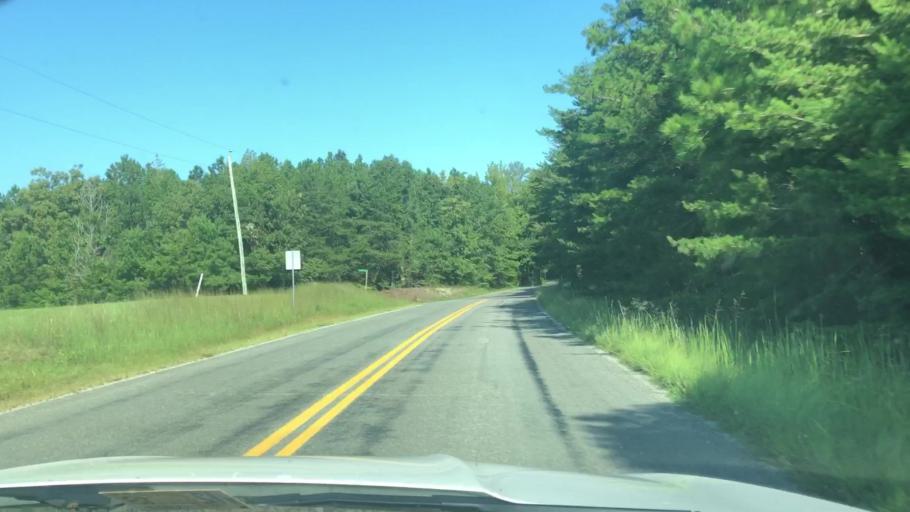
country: US
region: Virginia
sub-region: New Kent County
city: New Kent
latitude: 37.4864
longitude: -76.9326
